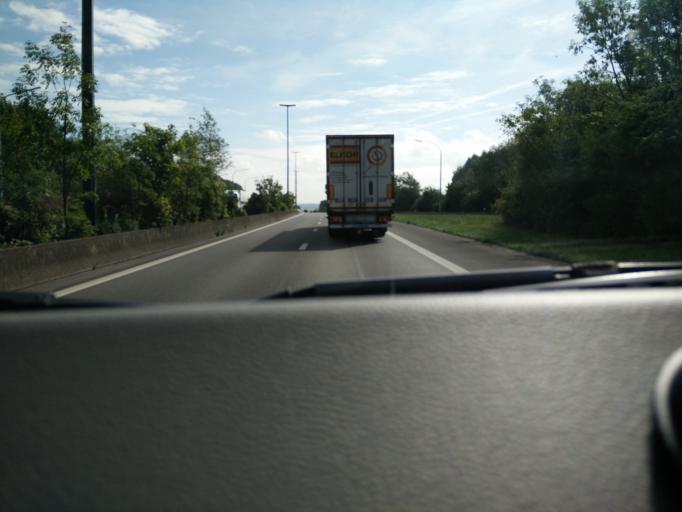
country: BE
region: Wallonia
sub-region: Province du Luxembourg
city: Wellin
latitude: 50.0937
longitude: 5.1379
